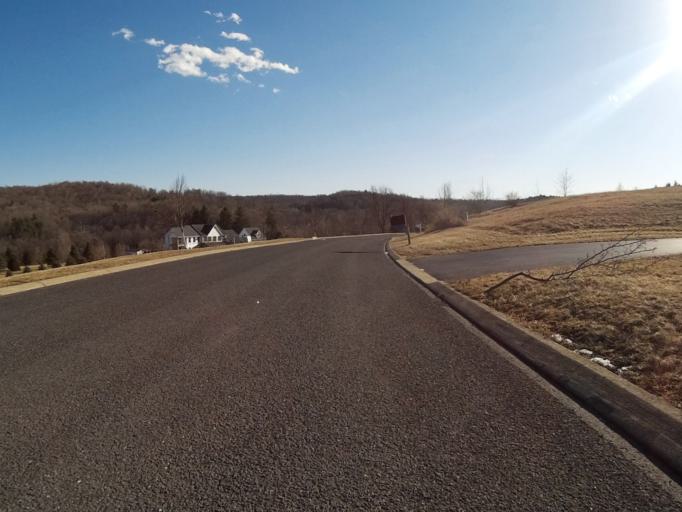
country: US
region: Pennsylvania
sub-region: Centre County
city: Park Forest Village
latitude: 40.8419
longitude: -77.9216
